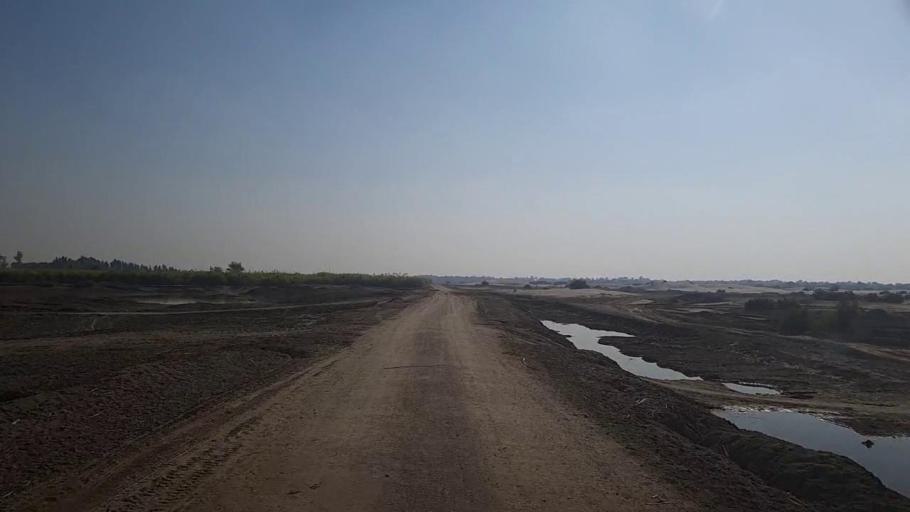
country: PK
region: Sindh
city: Kot Diji
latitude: 27.4375
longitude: 68.7278
